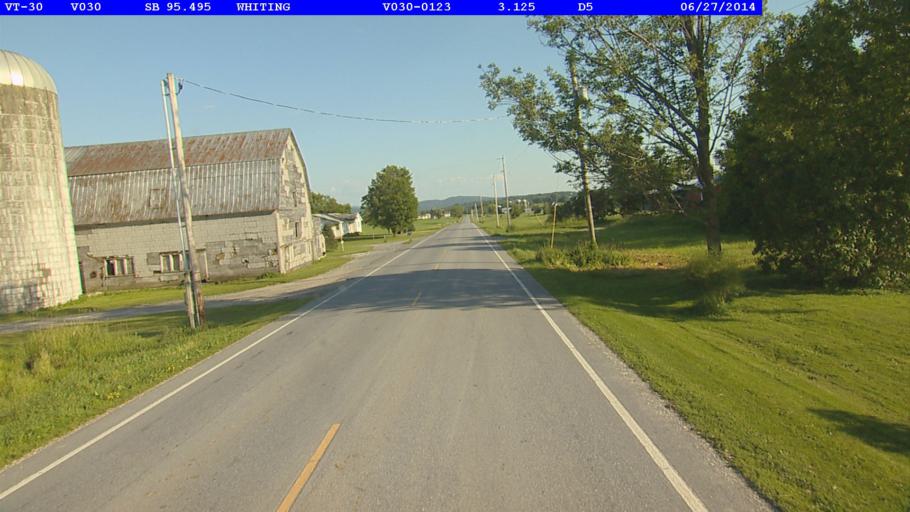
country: US
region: Vermont
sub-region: Addison County
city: Middlebury (village)
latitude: 43.8824
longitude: -73.2007
